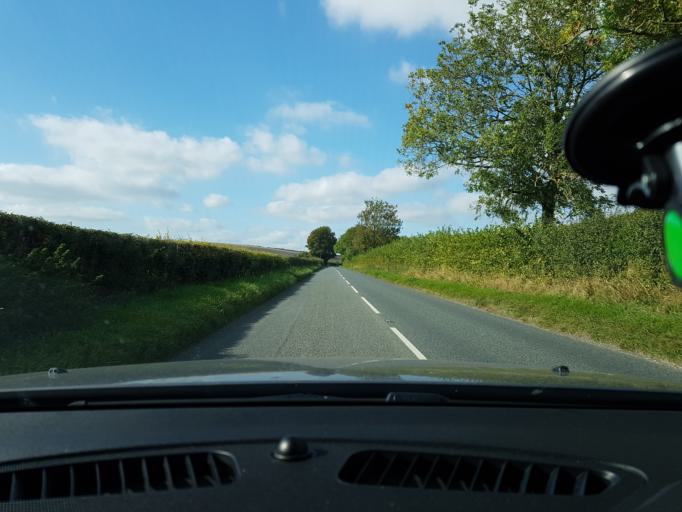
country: GB
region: England
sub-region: Wiltshire
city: Aldbourne
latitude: 51.4894
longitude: -1.6418
